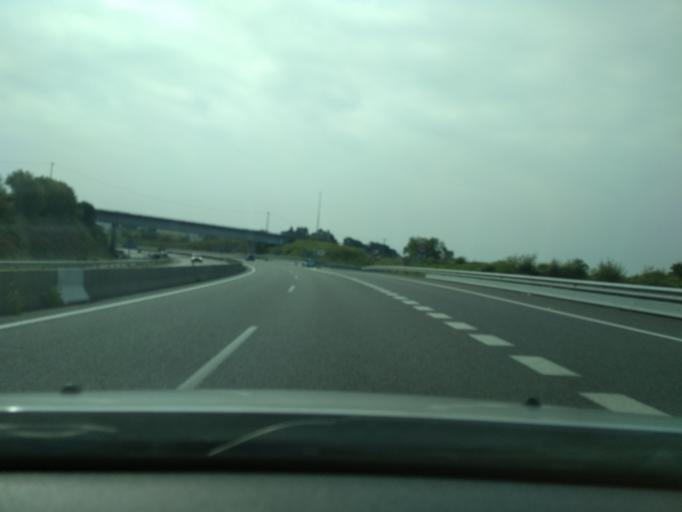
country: ES
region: Galicia
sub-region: Provincia da Coruna
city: Rianxo
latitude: 42.6708
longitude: -8.8285
